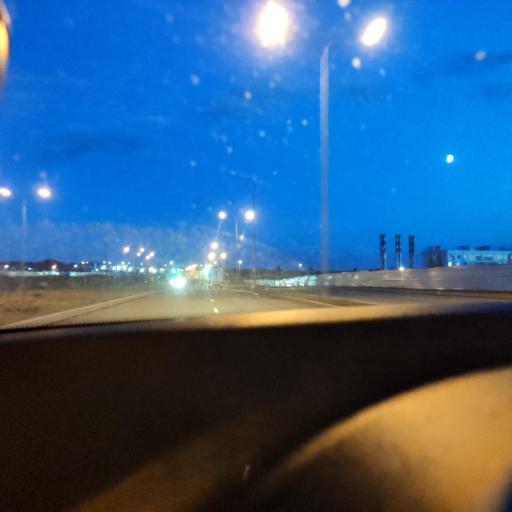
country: RU
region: Samara
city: Petra-Dubrava
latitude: 53.2972
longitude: 50.3223
